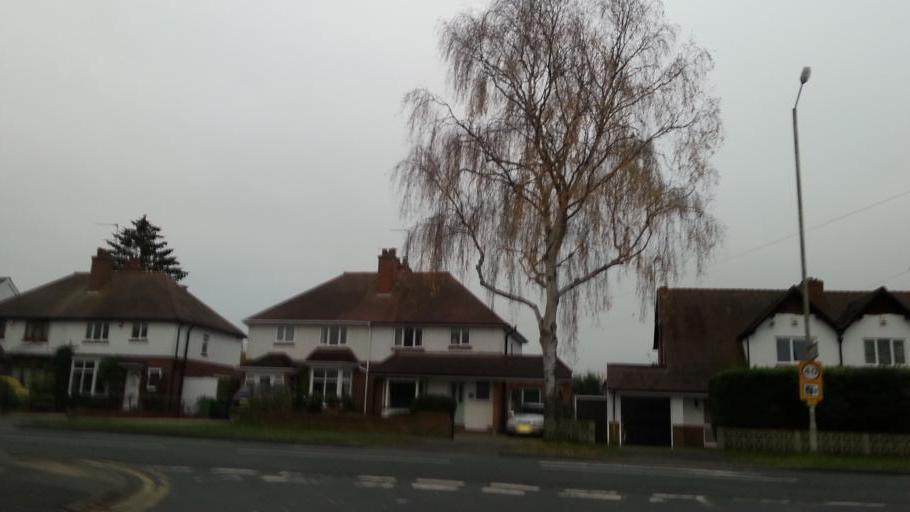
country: GB
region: England
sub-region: Dudley
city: Halesowen
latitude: 52.4399
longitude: -2.0723
